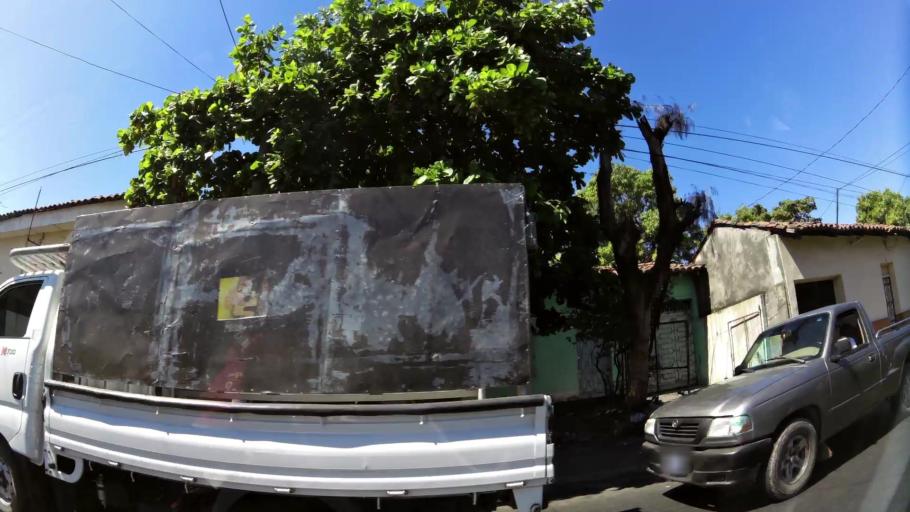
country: SV
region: San Miguel
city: San Miguel
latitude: 13.4786
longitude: -88.1719
